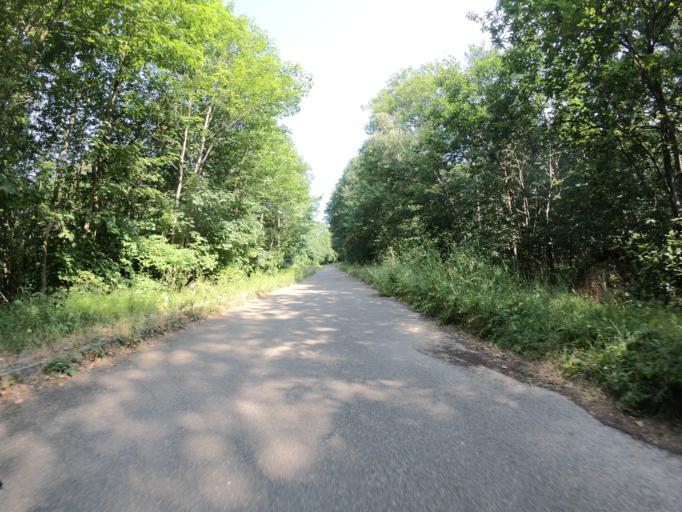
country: FR
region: Ile-de-France
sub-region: Departement de l'Essonne
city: Igny
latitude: 48.7482
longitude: 2.2379
